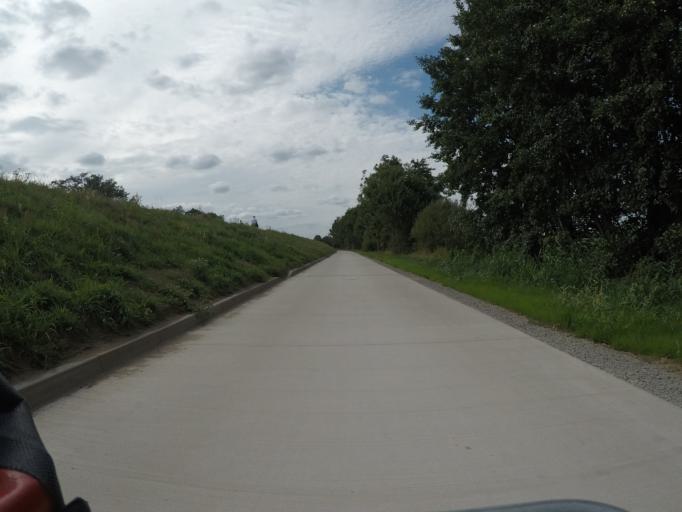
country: DE
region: Lower Saxony
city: Handorf
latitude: 53.3528
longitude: 10.3707
